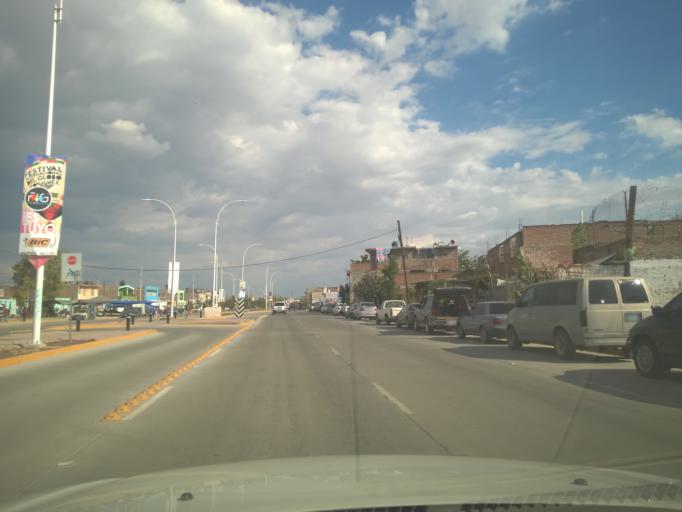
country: MX
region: Guanajuato
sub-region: Leon
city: San Jose de Duran (Los Troncoso)
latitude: 21.0639
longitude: -101.6290
